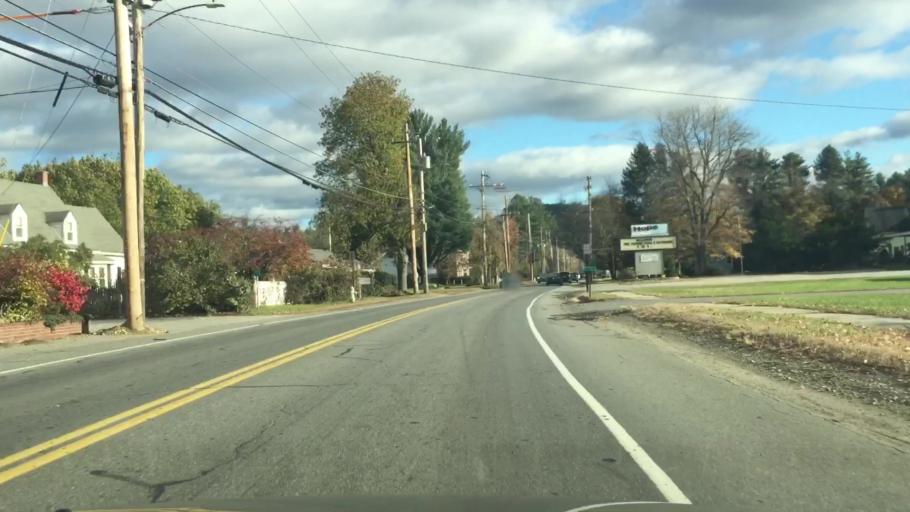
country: US
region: New Hampshire
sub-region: Cheshire County
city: Keene
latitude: 42.9137
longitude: -72.2676
